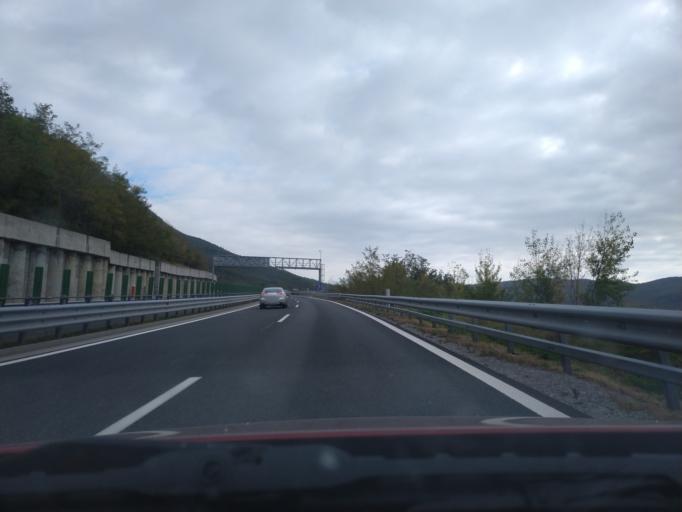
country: SI
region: Vipava
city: Vipava
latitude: 45.7811
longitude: 14.0128
